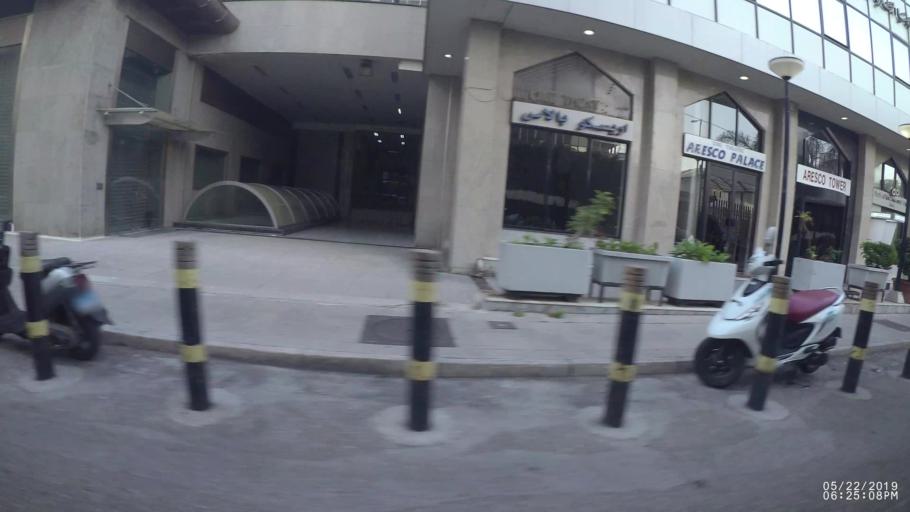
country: LB
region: Beyrouth
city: Beirut
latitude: 33.8958
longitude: 35.4910
